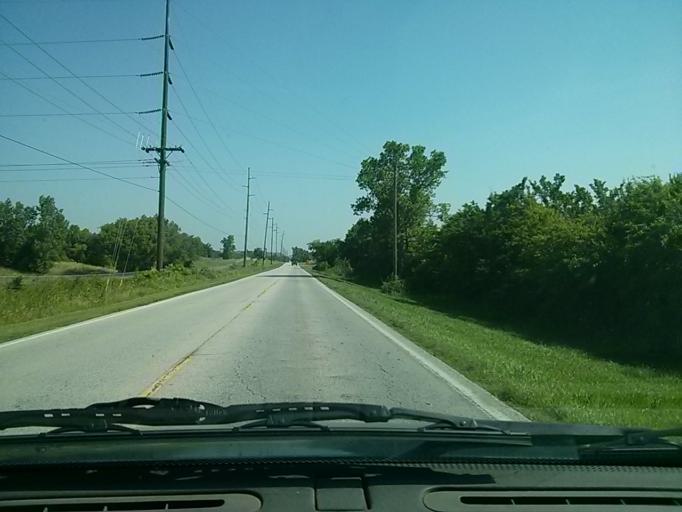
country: US
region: Oklahoma
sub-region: Rogers County
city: Catoosa
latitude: 36.1375
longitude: -95.7617
